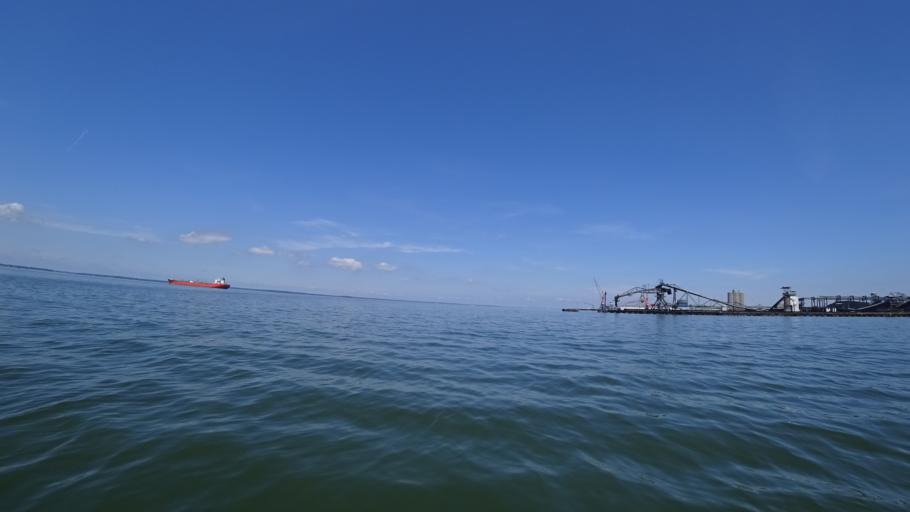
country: US
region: Virginia
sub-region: City of Newport News
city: Newport News
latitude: 36.9602
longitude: -76.4209
